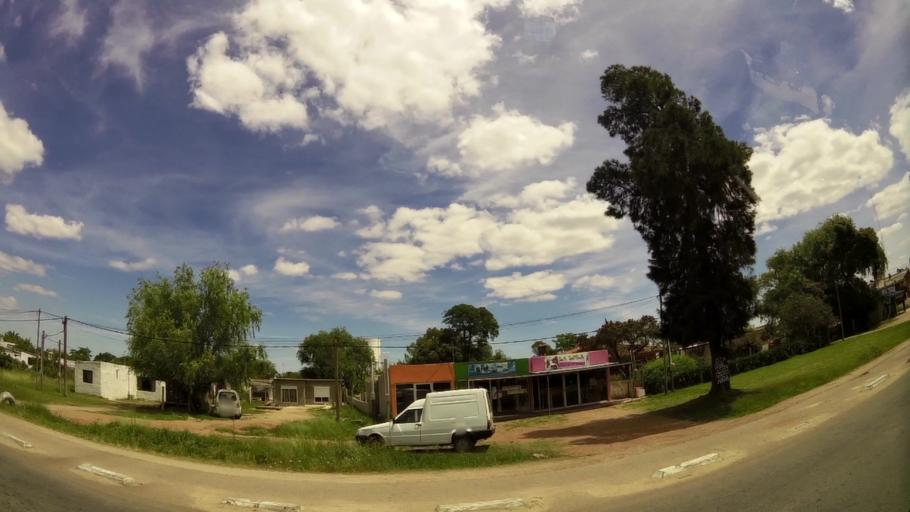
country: UY
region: San Jose
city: Delta del Tigre
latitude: -34.7500
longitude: -56.4188
